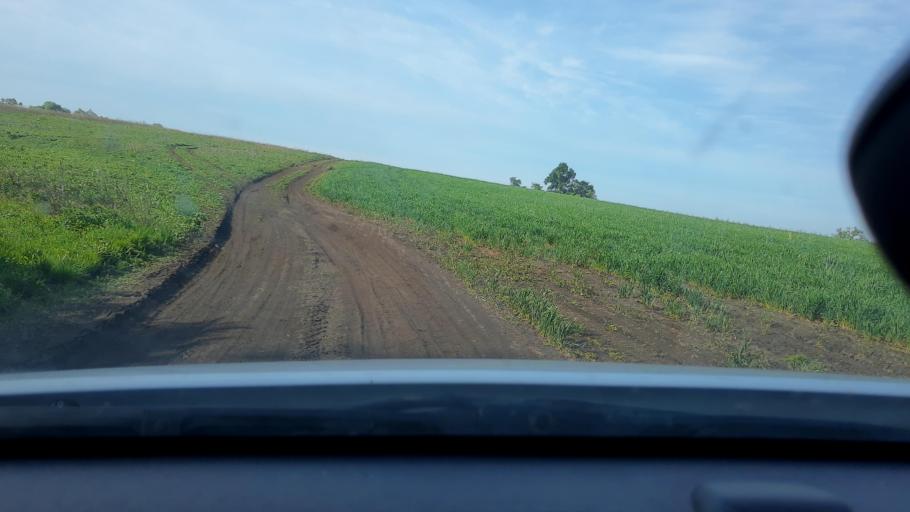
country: RU
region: Bashkortostan
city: Avdon
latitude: 54.7017
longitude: 55.7806
